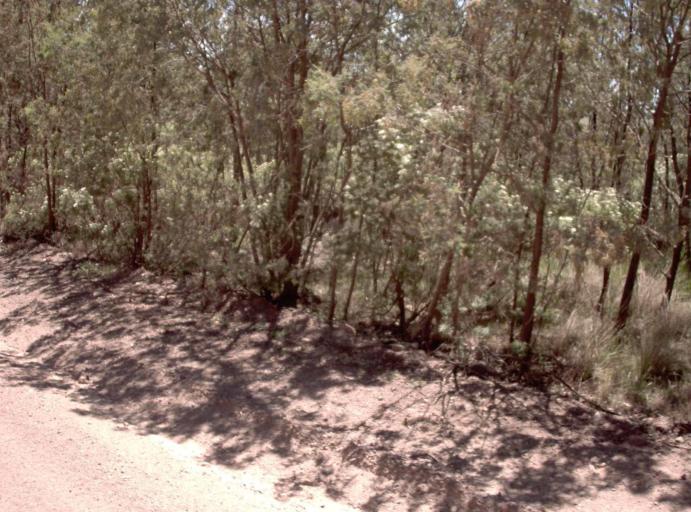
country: AU
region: New South Wales
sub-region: Snowy River
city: Jindabyne
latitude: -37.0260
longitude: 148.2735
